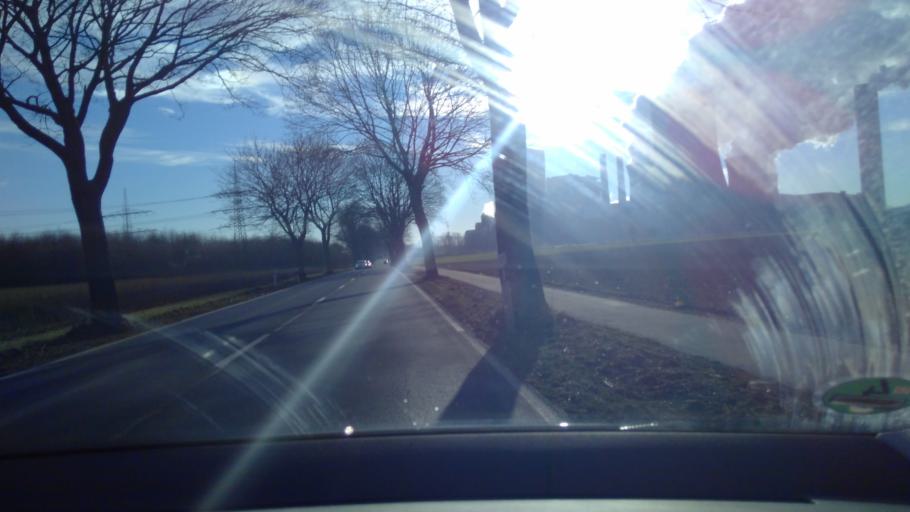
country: DE
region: North Rhine-Westphalia
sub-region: Regierungsbezirk Dusseldorf
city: Rommerskirchen
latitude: 51.0037
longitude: 6.6826
